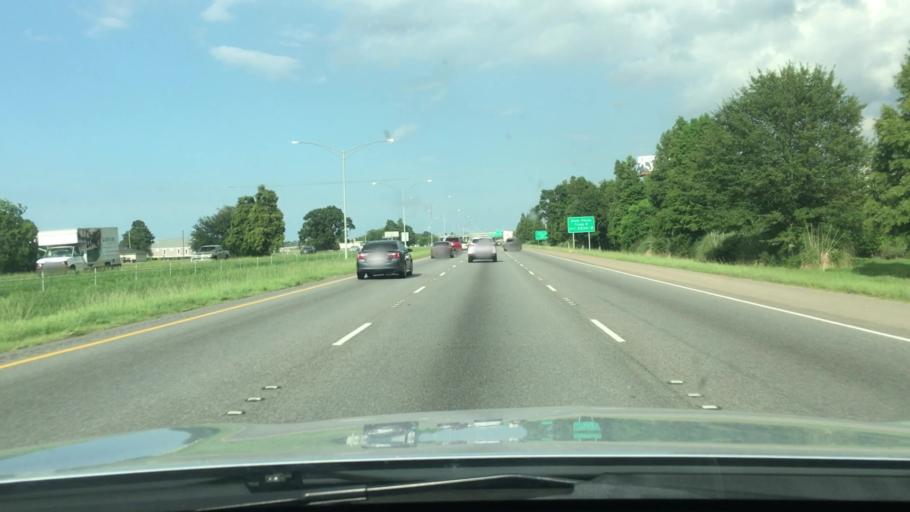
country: US
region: Louisiana
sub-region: Jefferson Parish
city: Kenner
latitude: 30.0086
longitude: -90.2529
